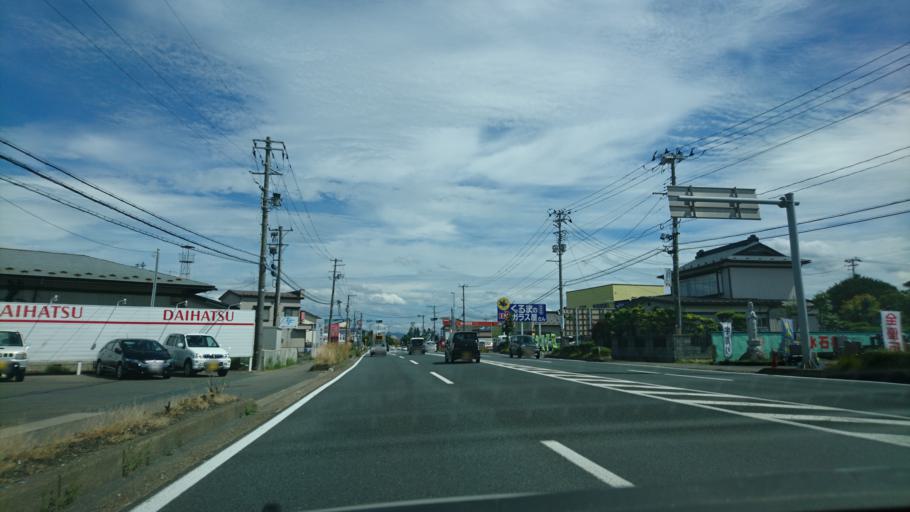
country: JP
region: Iwate
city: Morioka-shi
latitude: 39.6380
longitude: 141.1705
